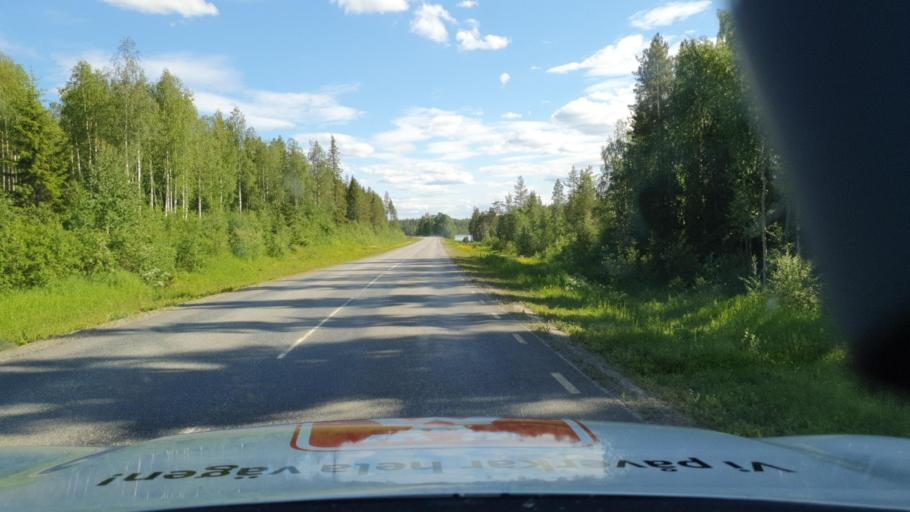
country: SE
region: Vaesterbotten
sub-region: Norsjo Kommun
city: Norsjoe
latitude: 64.8652
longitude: 19.7270
